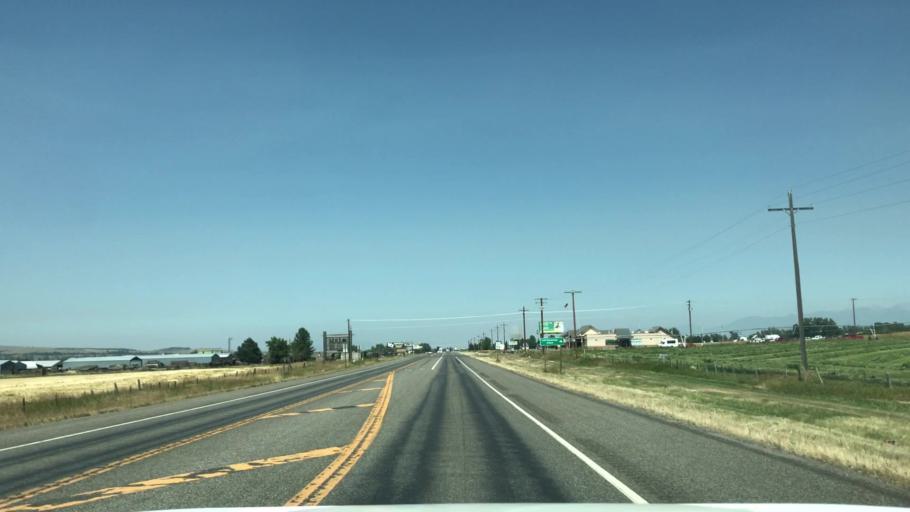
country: US
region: Montana
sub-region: Gallatin County
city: Four Corners
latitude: 45.5815
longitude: -111.1970
